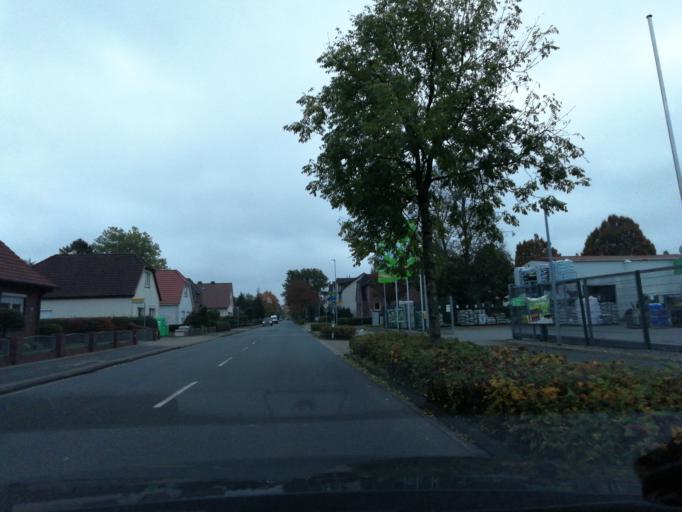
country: DE
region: Lower Saxony
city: Schortens
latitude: 53.5448
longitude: 7.9373
